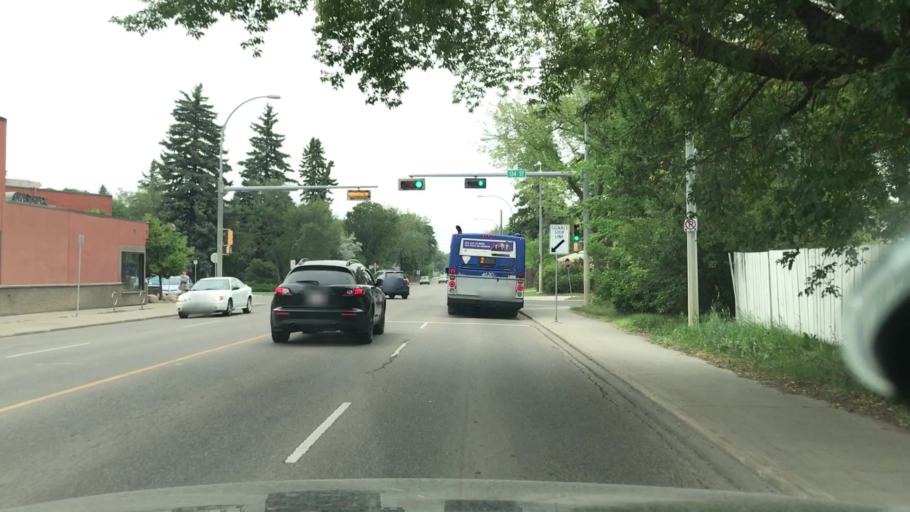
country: CA
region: Alberta
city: Edmonton
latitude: 53.5454
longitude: -113.5536
